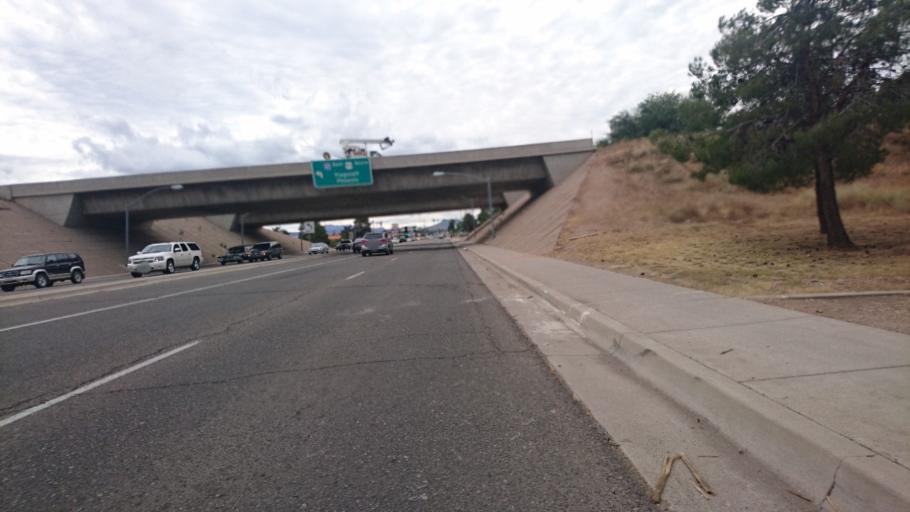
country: US
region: Arizona
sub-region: Mohave County
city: Kingman
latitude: 35.2180
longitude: -114.0356
